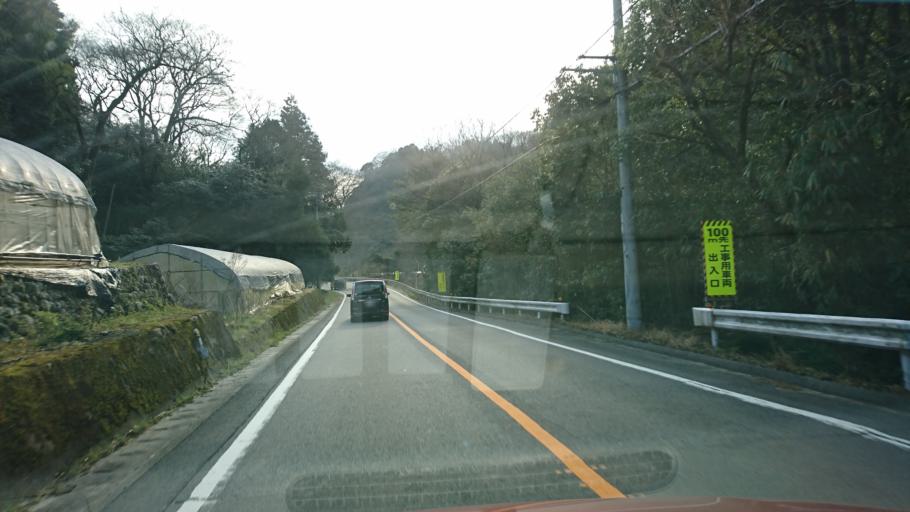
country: JP
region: Ehime
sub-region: Shikoku-chuo Shi
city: Matsuyama
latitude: 33.8963
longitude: 132.8444
